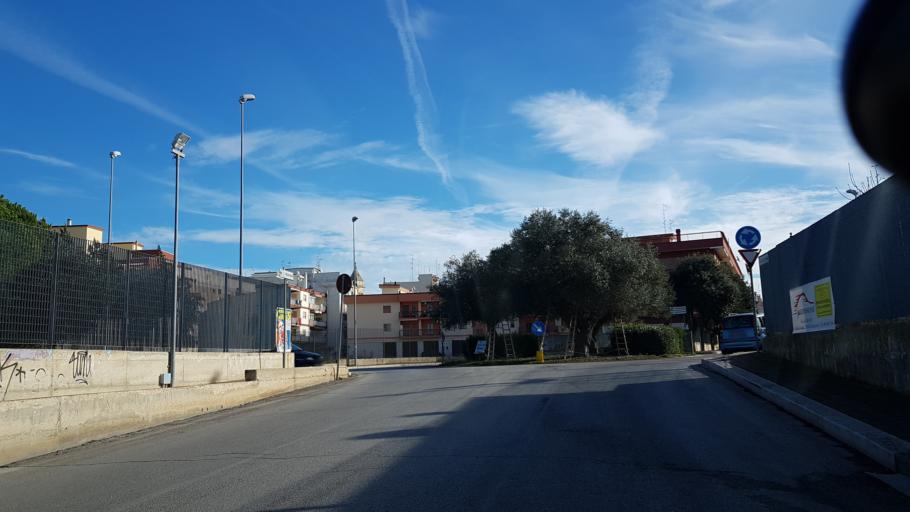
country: IT
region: Apulia
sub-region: Provincia di Bari
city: Gioia del Colle
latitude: 40.8005
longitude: 16.9175
